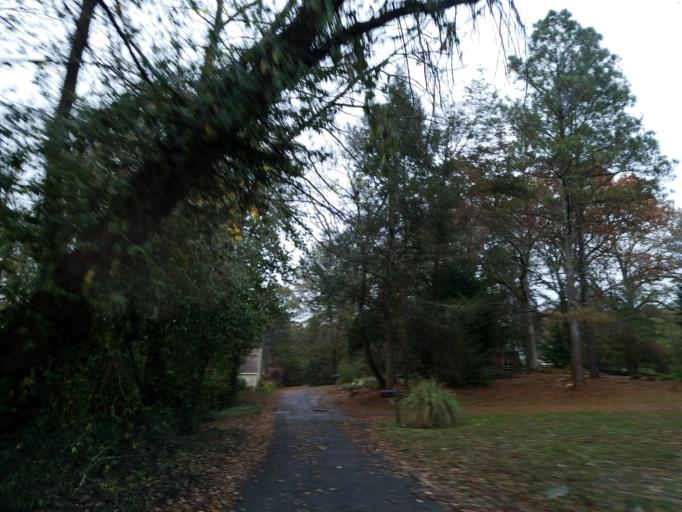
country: US
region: Georgia
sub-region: Cherokee County
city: Ball Ground
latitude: 34.3344
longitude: -84.3742
